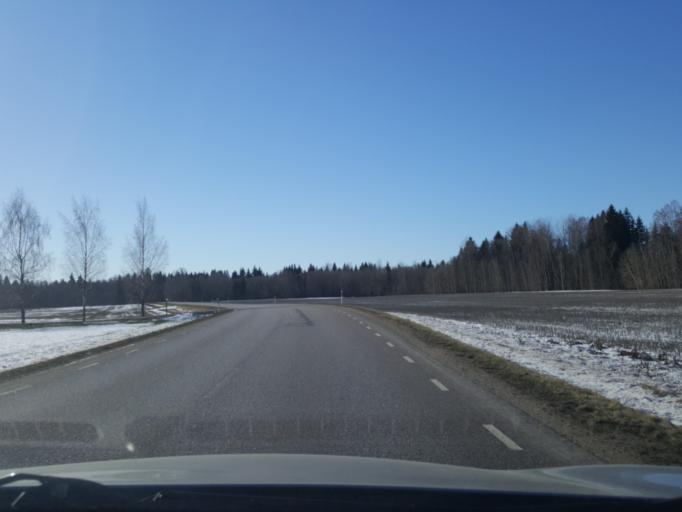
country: EE
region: Viljandimaa
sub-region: Viiratsi vald
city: Viiratsi
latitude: 58.4206
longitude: 25.6789
